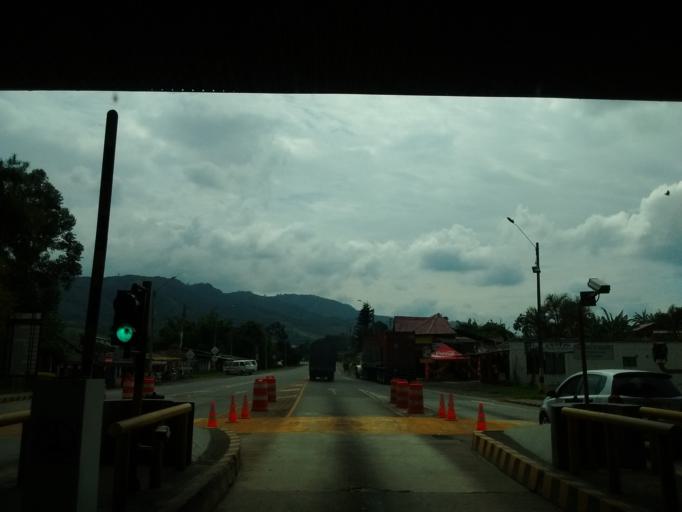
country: CO
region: Cauca
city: Cajibio
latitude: 2.7019
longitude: -76.5369
